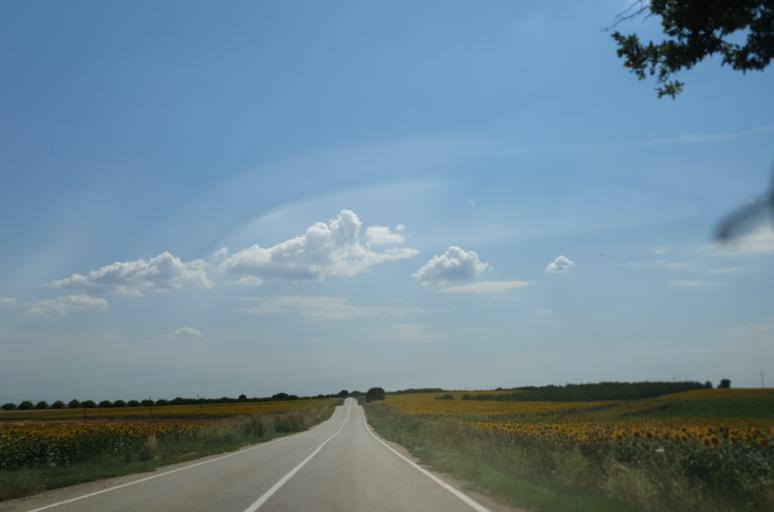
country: TR
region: Kirklareli
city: Vize
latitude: 41.4827
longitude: 27.6858
